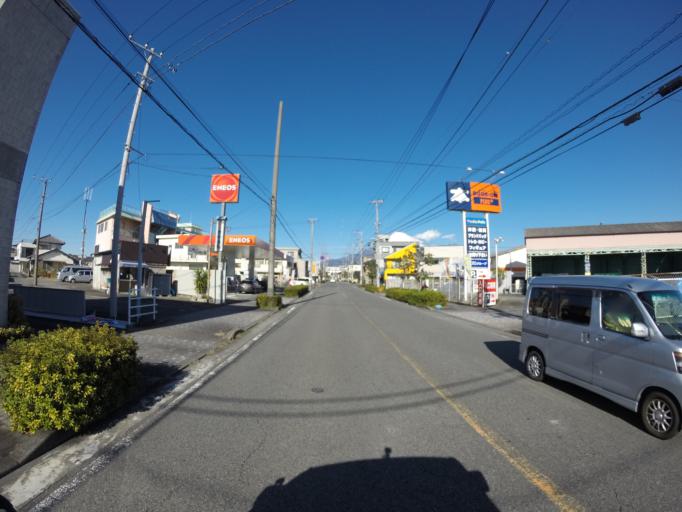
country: JP
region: Shizuoka
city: Fuji
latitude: 35.1623
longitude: 138.6534
